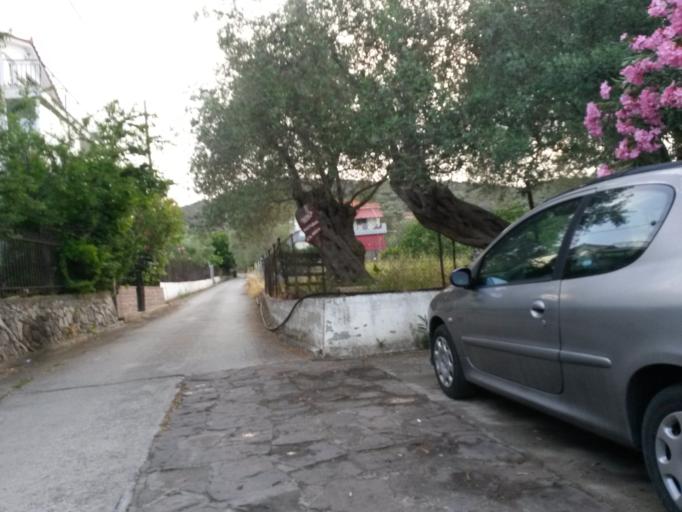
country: GR
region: North Aegean
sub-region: Nomos Lesvou
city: Pamfylla
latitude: 39.1728
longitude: 26.5010
